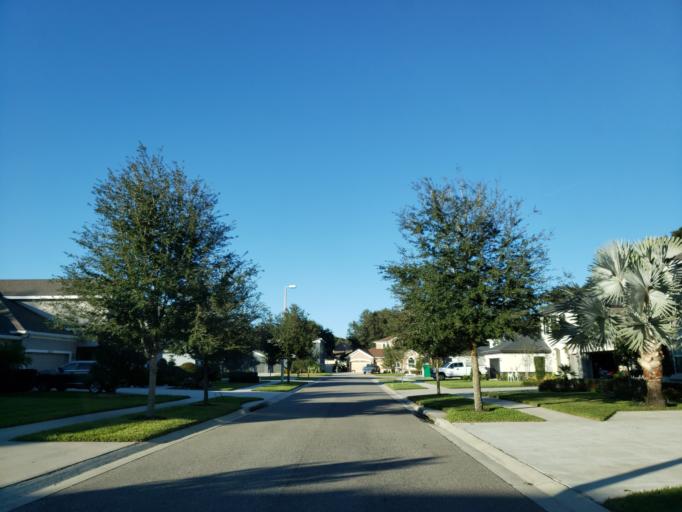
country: US
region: Florida
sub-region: Hillsborough County
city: Bloomingdale
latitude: 27.8961
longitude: -82.2386
